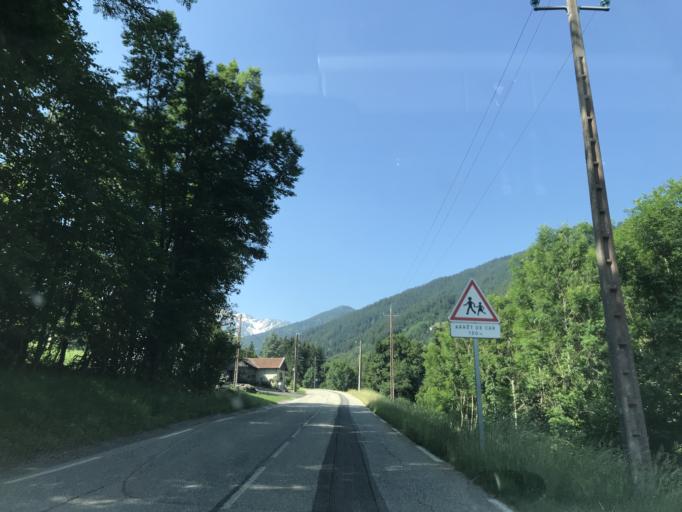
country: FR
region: Rhone-Alpes
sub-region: Departement de l'Isere
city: Allevard
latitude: 45.3135
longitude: 6.0829
